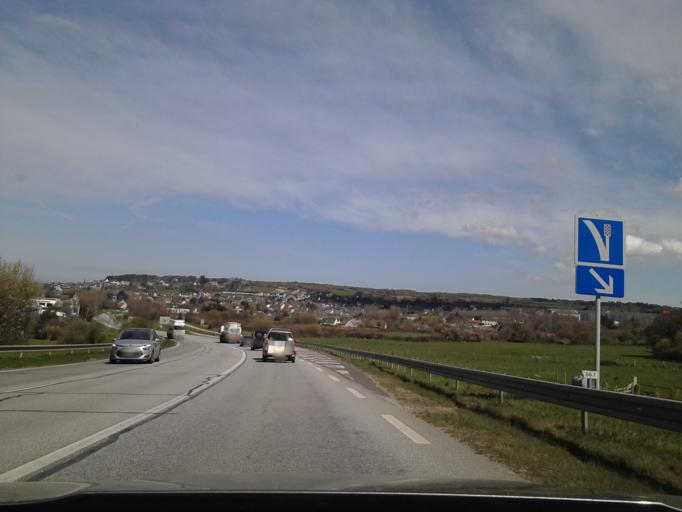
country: FR
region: Lower Normandy
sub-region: Departement de la Manche
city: Tourlaville
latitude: 49.6304
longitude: -1.5796
